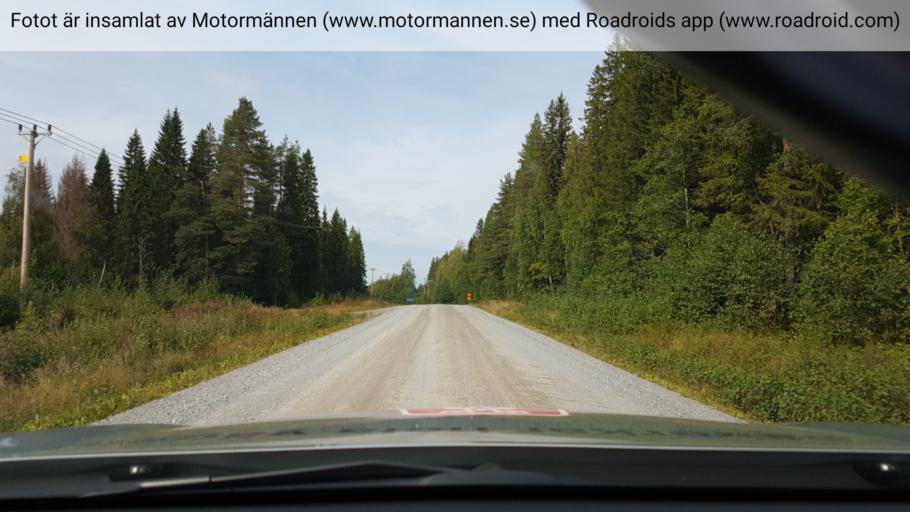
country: SE
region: Vaesterbotten
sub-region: Bjurholms Kommun
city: Bjurholm
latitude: 63.9299
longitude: 19.3596
